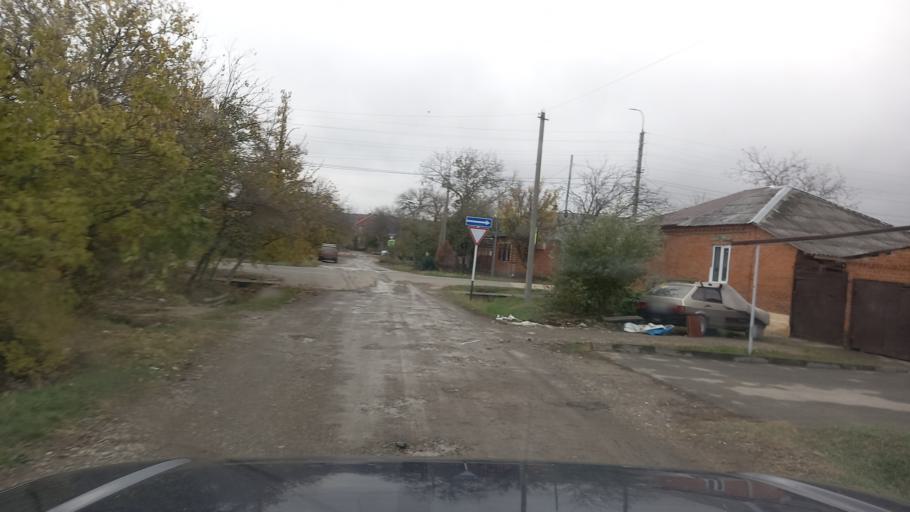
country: RU
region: Adygeya
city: Maykop
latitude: 44.6033
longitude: 40.0855
